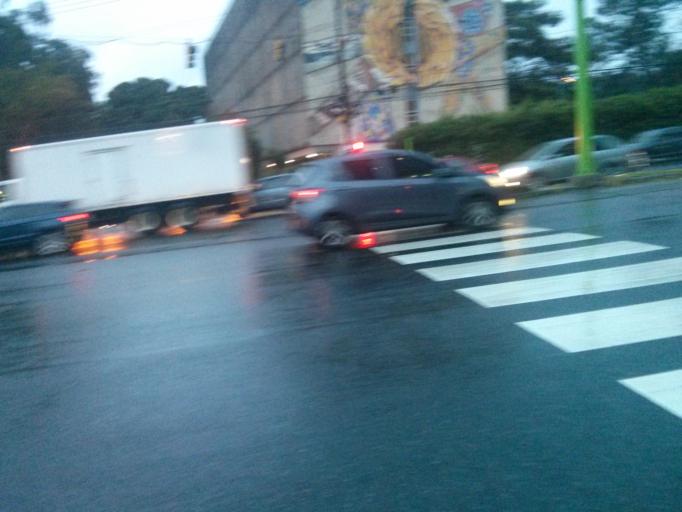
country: CR
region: San Jose
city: San Pedro
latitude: 9.9367
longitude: -84.0545
